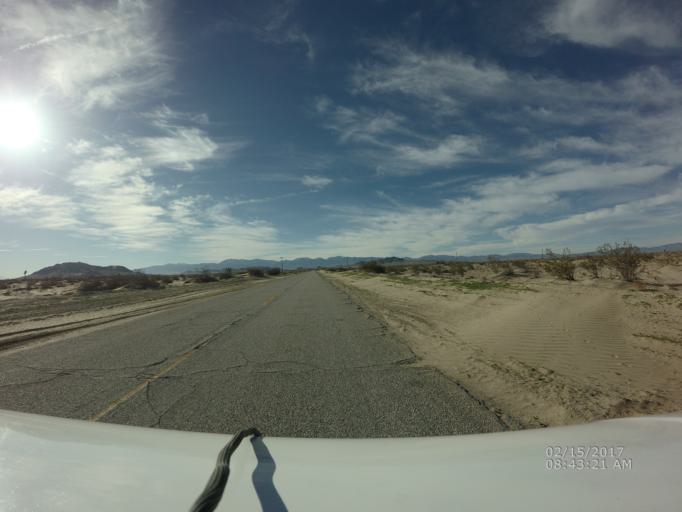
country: US
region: California
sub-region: Los Angeles County
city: Lake Los Angeles
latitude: 34.6840
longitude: -117.8808
